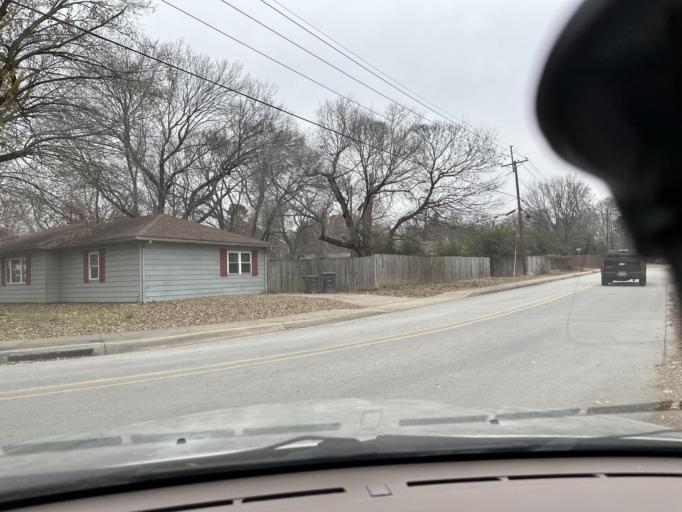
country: US
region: Arkansas
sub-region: Washington County
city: Johnson
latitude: 36.1097
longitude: -94.1406
